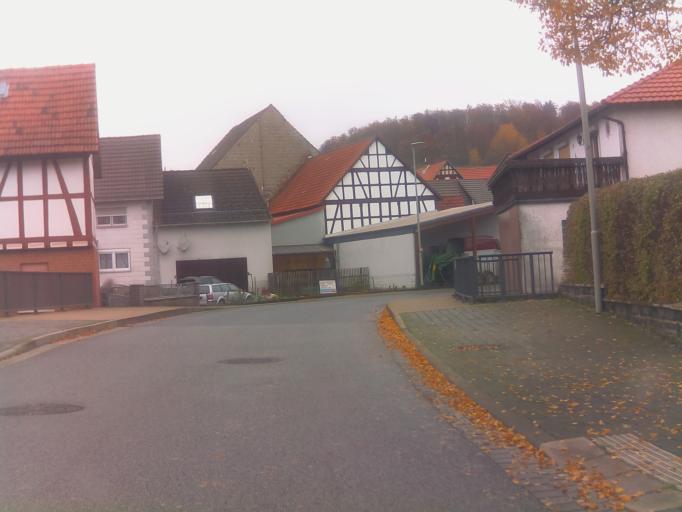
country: DE
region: Hesse
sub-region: Regierungsbezirk Darmstadt
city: Hirzenhain
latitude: 50.4182
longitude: 9.1330
